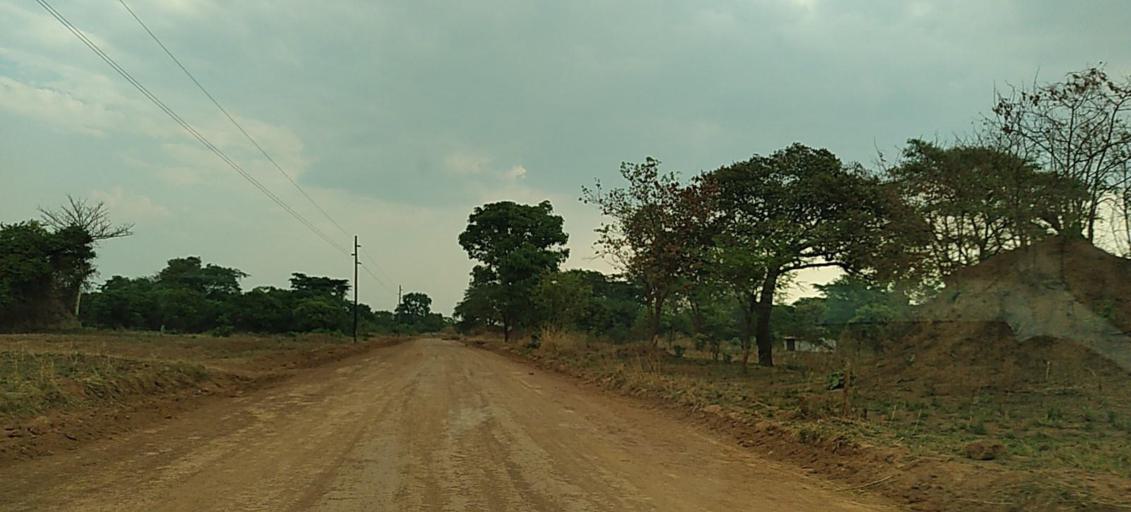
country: ZM
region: Copperbelt
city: Kalulushi
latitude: -12.9123
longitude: 27.9456
